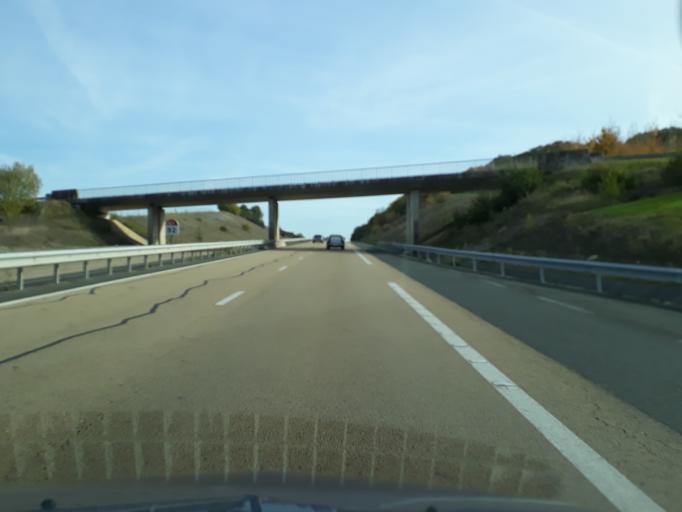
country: FR
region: Champagne-Ardenne
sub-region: Departement de l'Aube
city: Aix-en-Othe
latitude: 48.2572
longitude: 3.6430
